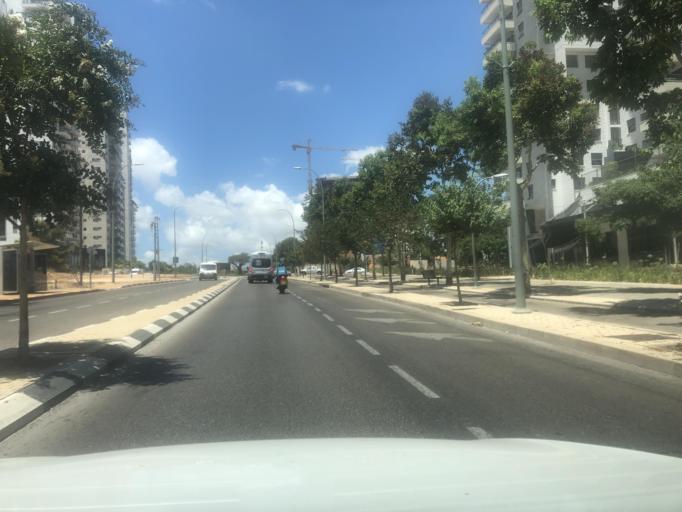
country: IL
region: Central District
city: Hod HaSharon
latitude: 32.1652
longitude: 34.9020
